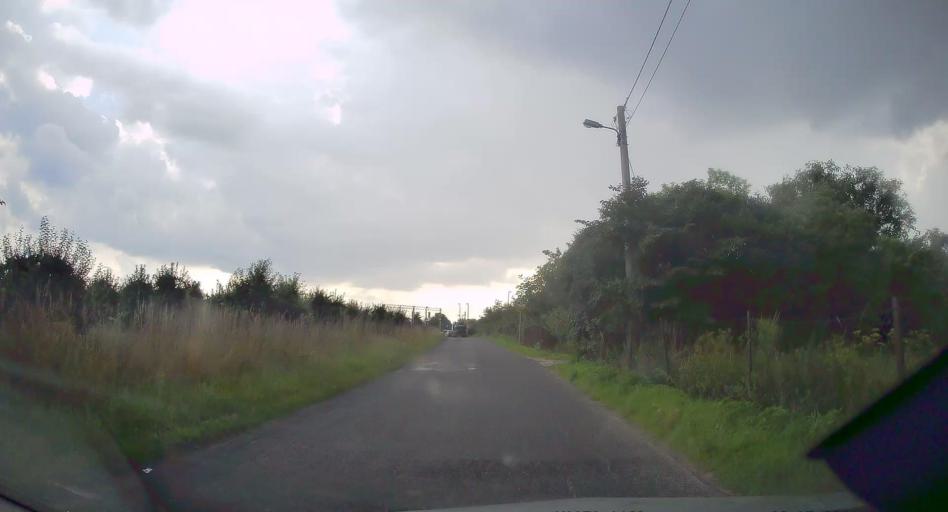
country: PL
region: Lodz Voivodeship
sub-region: Powiat brzezinski
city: Rogow
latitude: 51.8222
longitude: 19.8940
